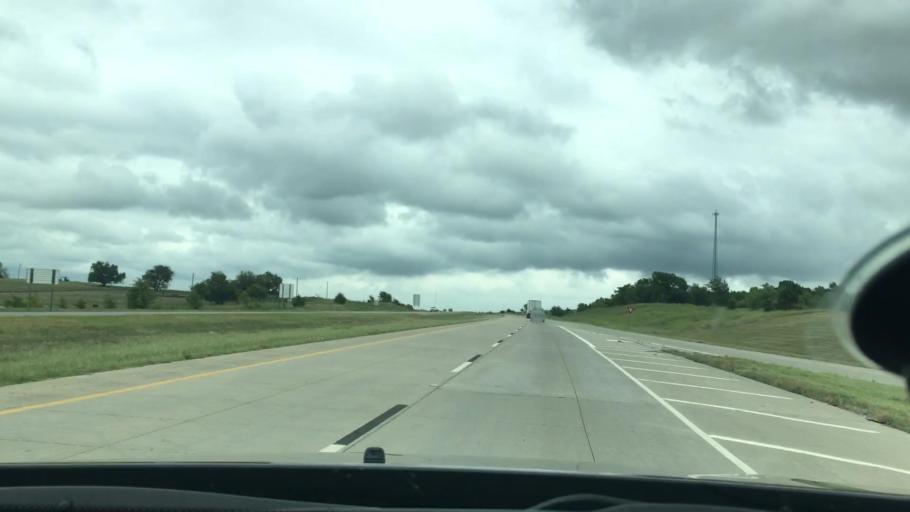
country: US
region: Oklahoma
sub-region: Bryan County
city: Durant
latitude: 34.1344
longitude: -96.2720
